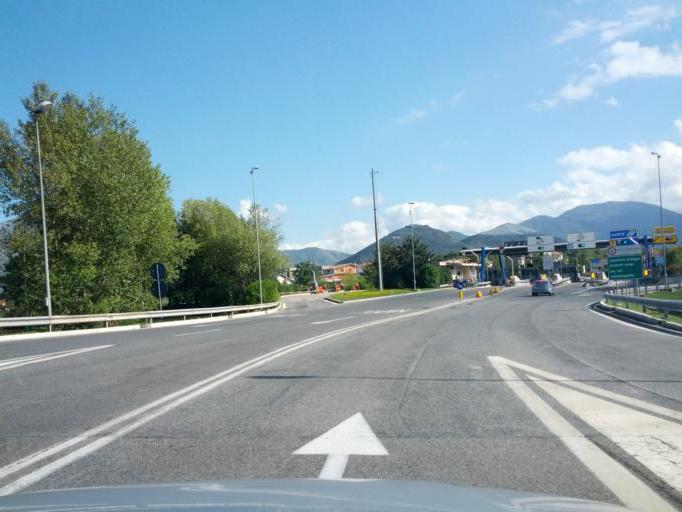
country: IT
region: Campania
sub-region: Provincia di Caserta
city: Bivio Mortola
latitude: 41.4335
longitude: 13.8995
